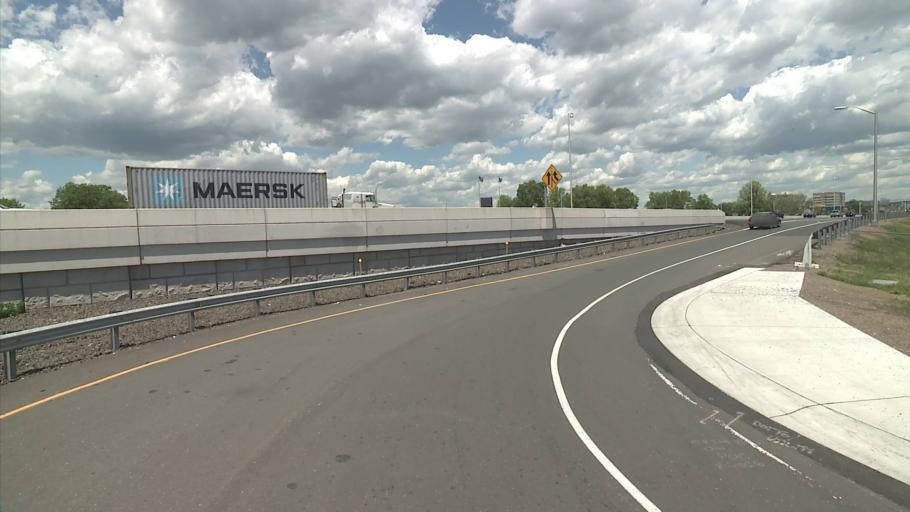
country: US
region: Connecticut
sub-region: New Haven County
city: New Haven
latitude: 41.2894
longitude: -72.9225
